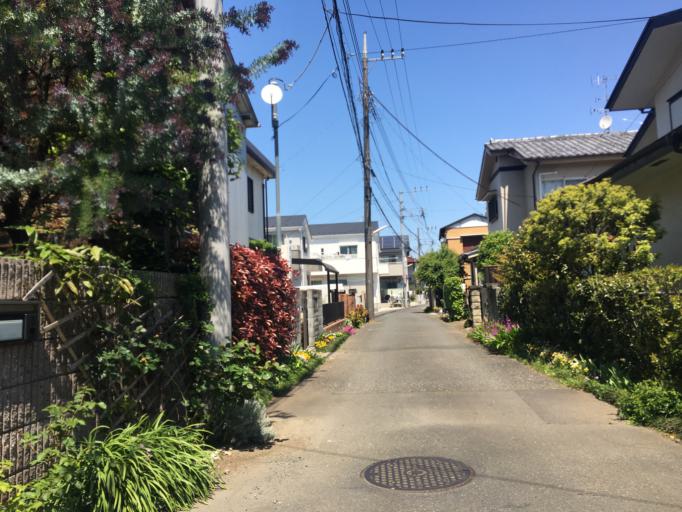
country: JP
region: Tokyo
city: Tanashicho
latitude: 35.7210
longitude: 139.5144
